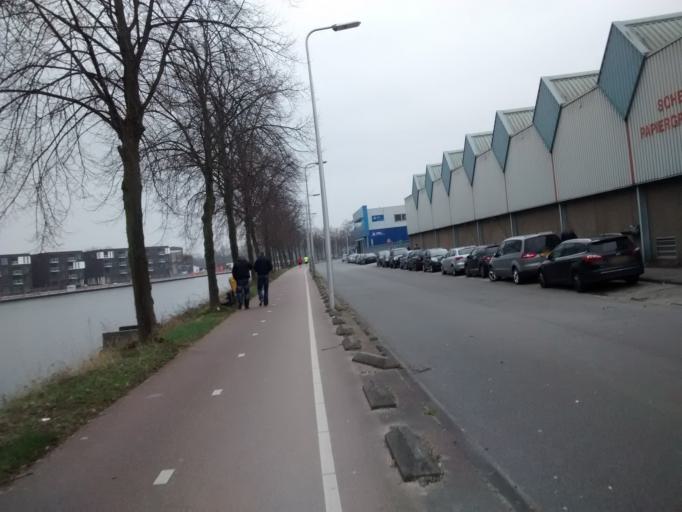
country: NL
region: Utrecht
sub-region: Gemeente Utrecht
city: Lunetten
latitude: 52.0651
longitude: 5.1121
